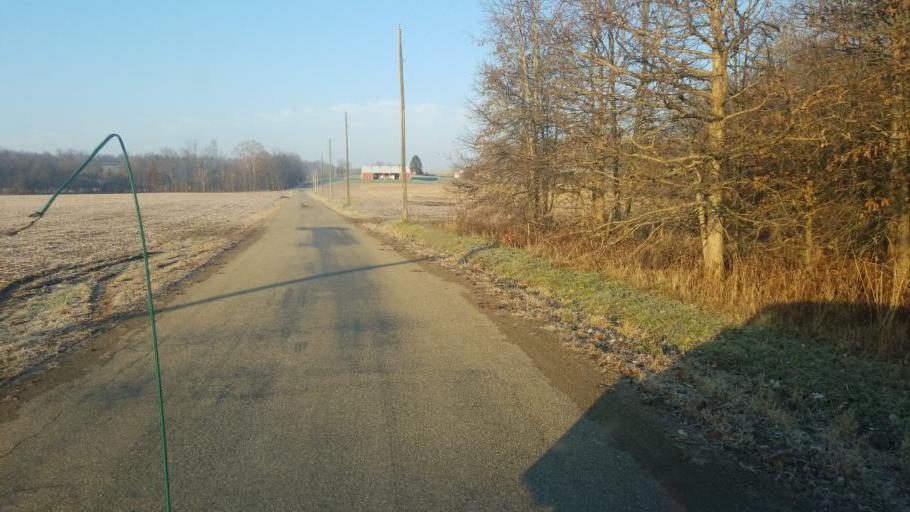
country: US
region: Ohio
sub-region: Knox County
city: Danville
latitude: 40.4460
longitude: -82.2997
